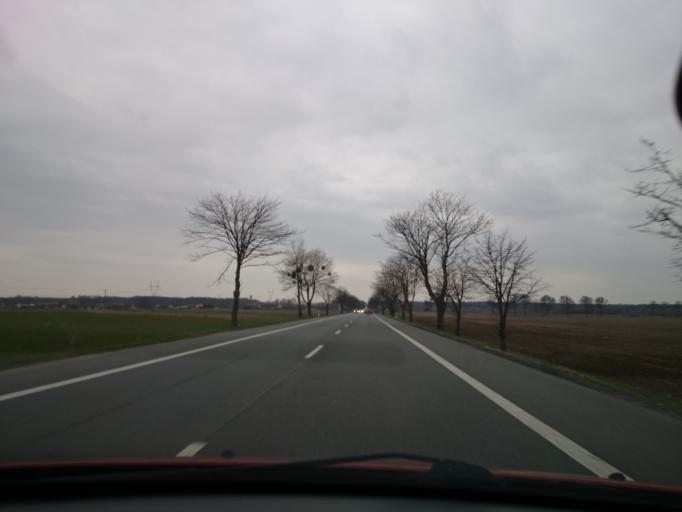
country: PL
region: Opole Voivodeship
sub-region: Powiat opolski
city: Niemodlin
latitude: 50.6245
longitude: 17.5795
